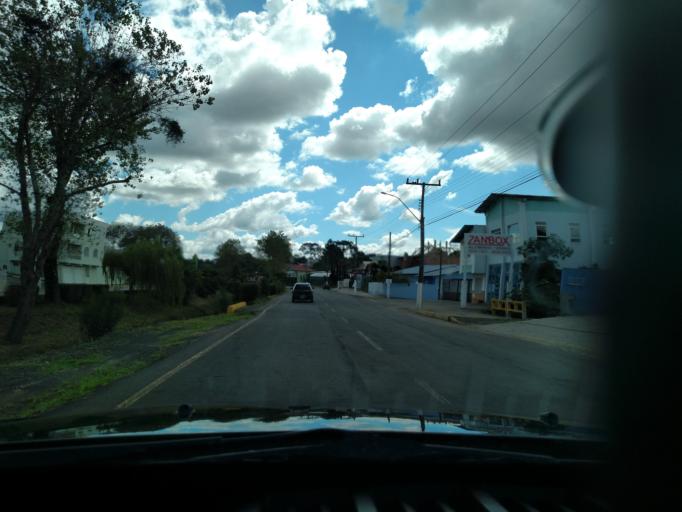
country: BR
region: Santa Catarina
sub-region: Lages
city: Lages
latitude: -27.8129
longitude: -50.3343
